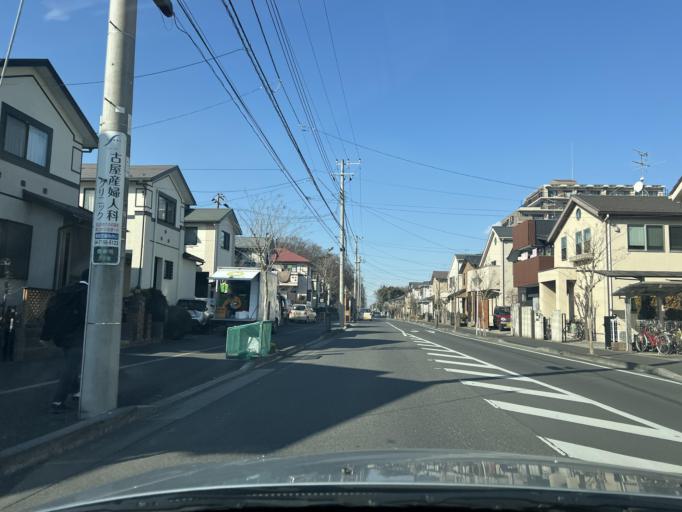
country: JP
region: Chiba
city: Nagareyama
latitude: 35.8850
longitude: 139.9131
